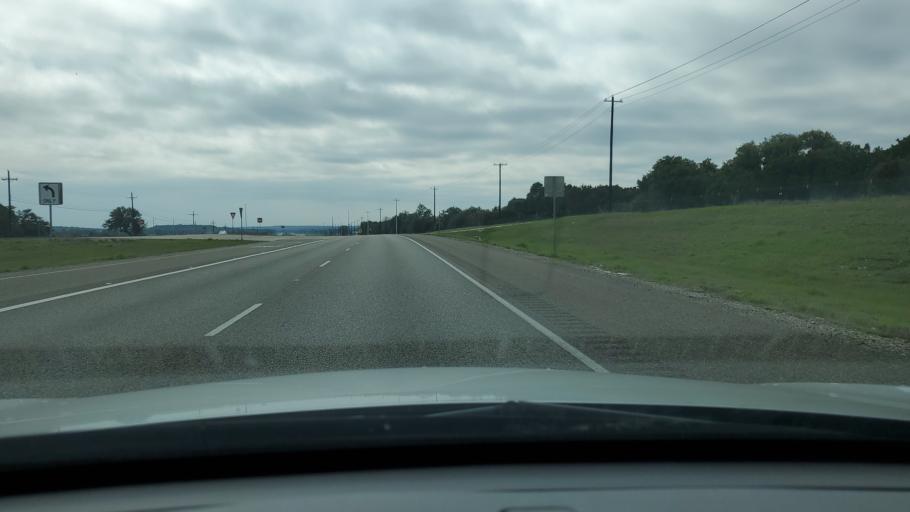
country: US
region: Texas
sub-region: Williamson County
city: Florence
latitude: 30.7946
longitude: -97.7673
